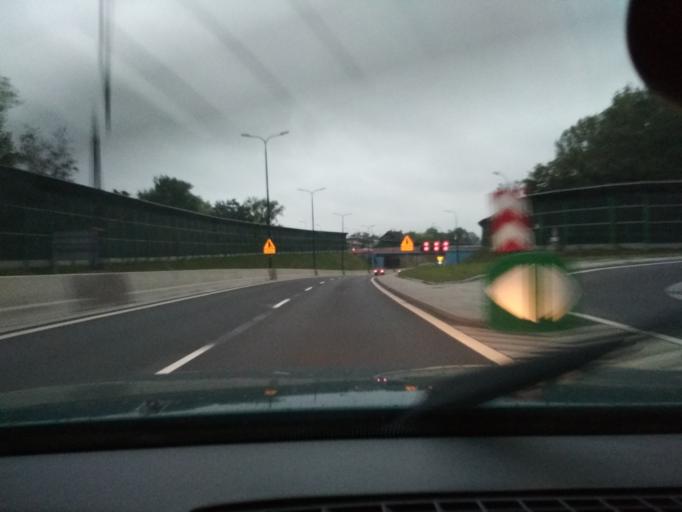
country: PL
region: Silesian Voivodeship
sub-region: Gliwice
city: Gliwice
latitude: 50.2912
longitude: 18.6937
